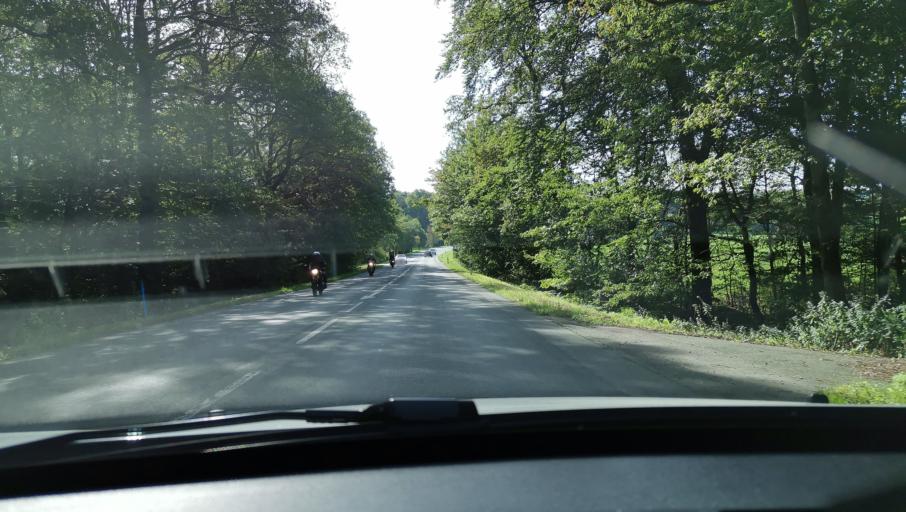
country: DE
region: North Rhine-Westphalia
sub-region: Regierungsbezirk Arnsberg
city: Breckerfeld
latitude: 51.2384
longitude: 7.4695
